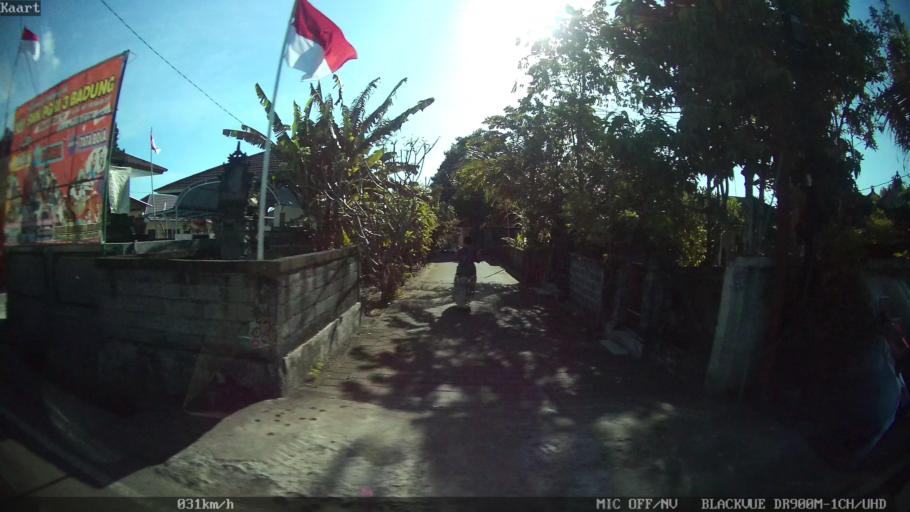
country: ID
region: Bali
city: Banjar Gunungpande
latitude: -8.6353
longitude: 115.1738
